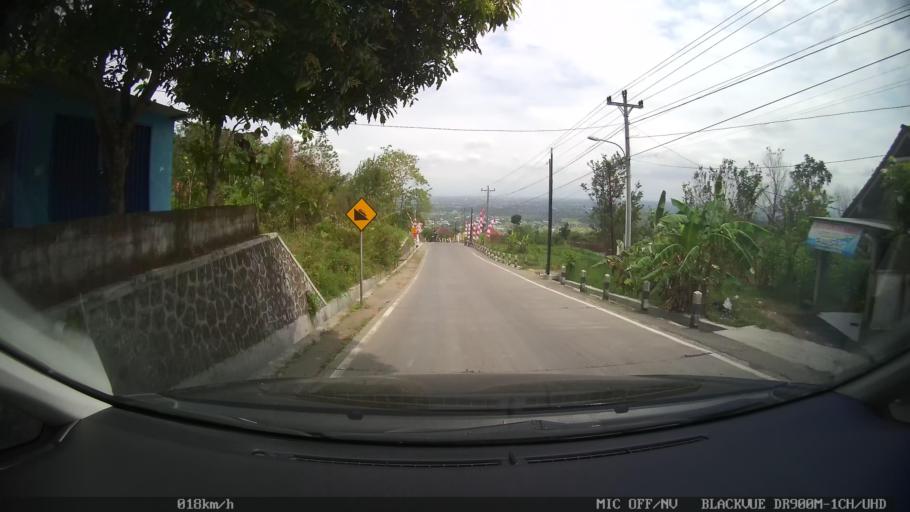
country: ID
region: Central Java
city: Candi Prambanan
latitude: -7.7835
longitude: 110.5038
